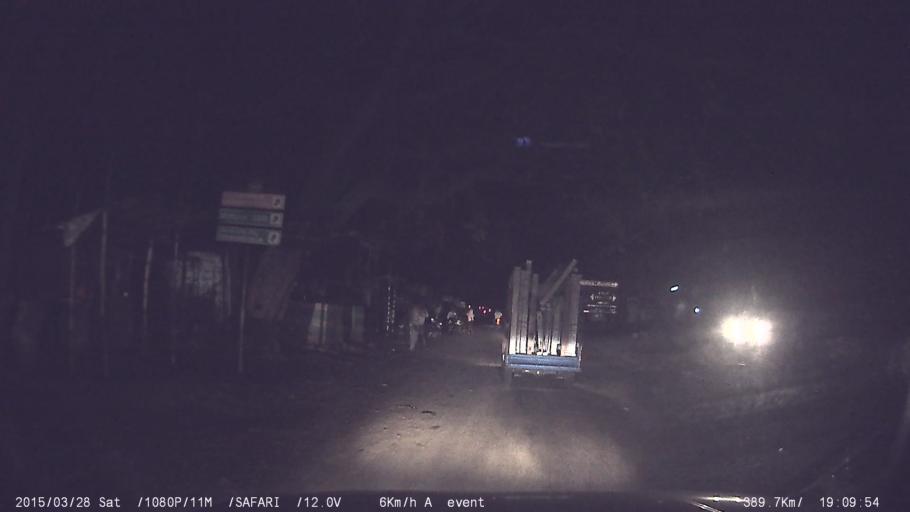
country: IN
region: Karnataka
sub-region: Mandya
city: Shrirangapattana
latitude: 12.3924
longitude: 76.6264
